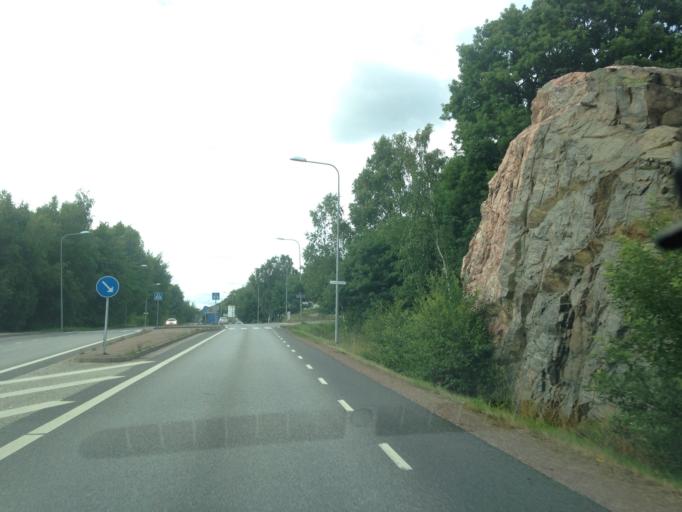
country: SE
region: Vaestra Goetaland
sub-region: Goteborg
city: Goeteborg
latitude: 57.7436
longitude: 11.9528
